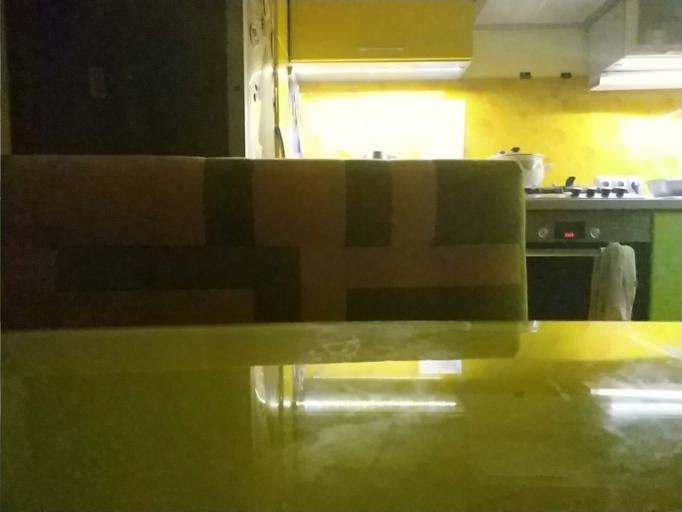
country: RU
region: Republic of Karelia
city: Pyaozerskiy
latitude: 65.8868
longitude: 30.4333
